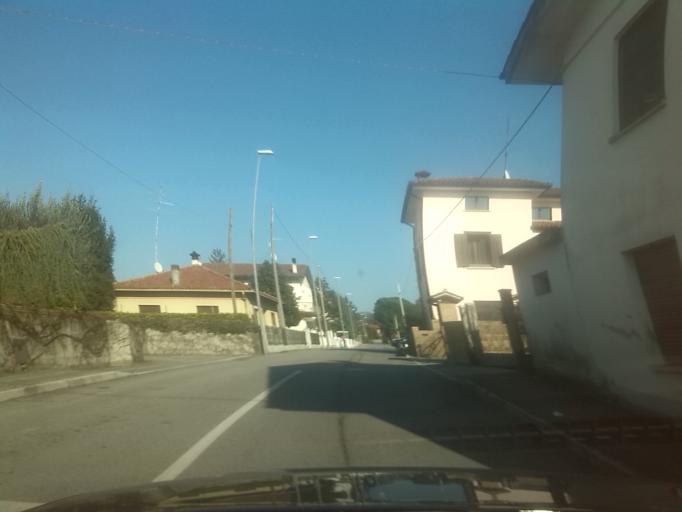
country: IT
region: Friuli Venezia Giulia
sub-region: Provincia di Udine
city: Manzano
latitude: 45.9928
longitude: 13.3927
